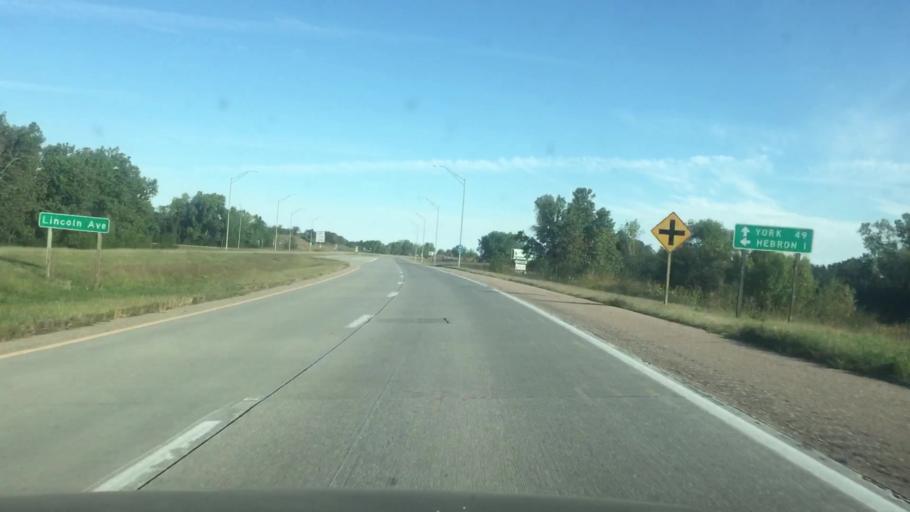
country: US
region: Nebraska
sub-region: Thayer County
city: Hebron
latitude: 40.1653
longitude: -97.5711
